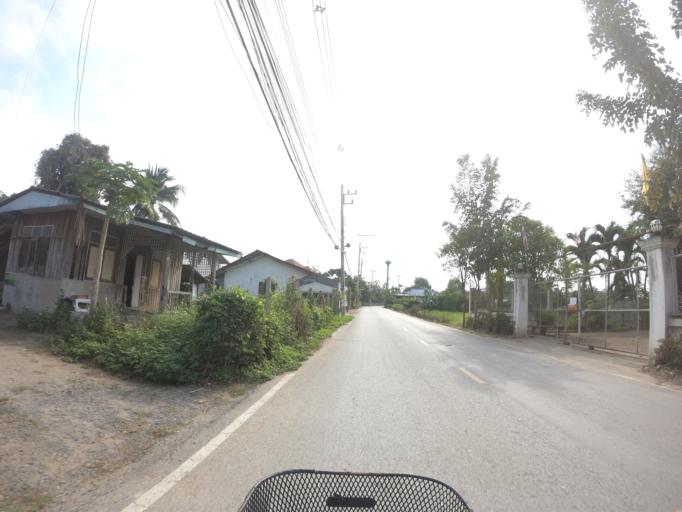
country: TH
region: Chiang Mai
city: Saraphi
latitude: 18.7306
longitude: 99.0612
